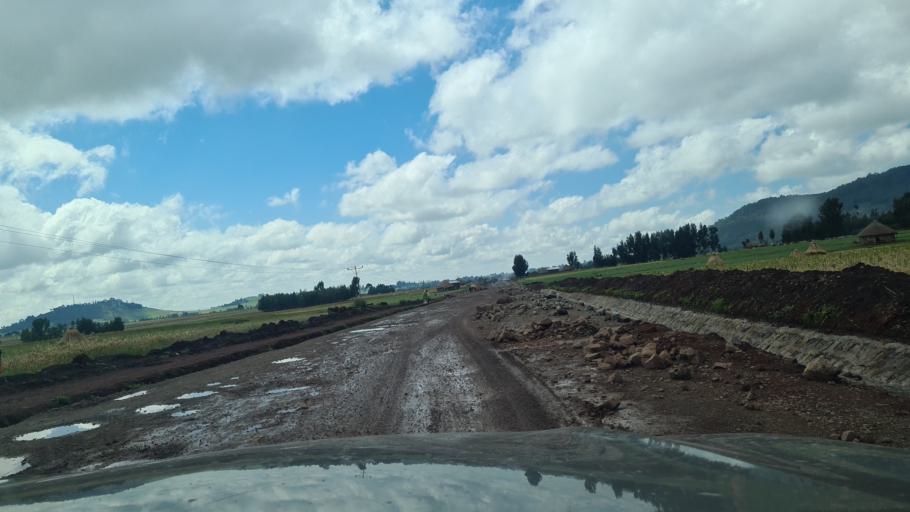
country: ET
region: Oromiya
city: Huruta
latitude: 8.0896
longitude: 39.5386
